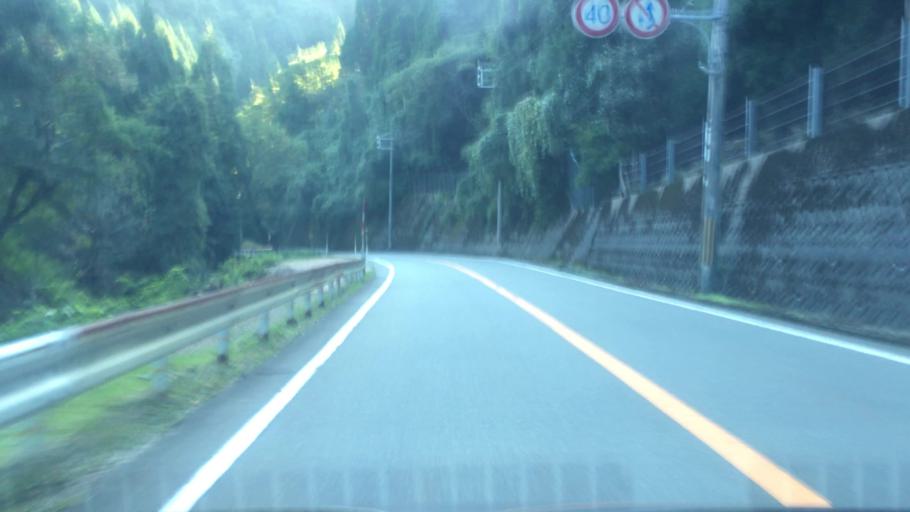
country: JP
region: Hyogo
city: Toyooka
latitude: 35.6178
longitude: 134.8590
